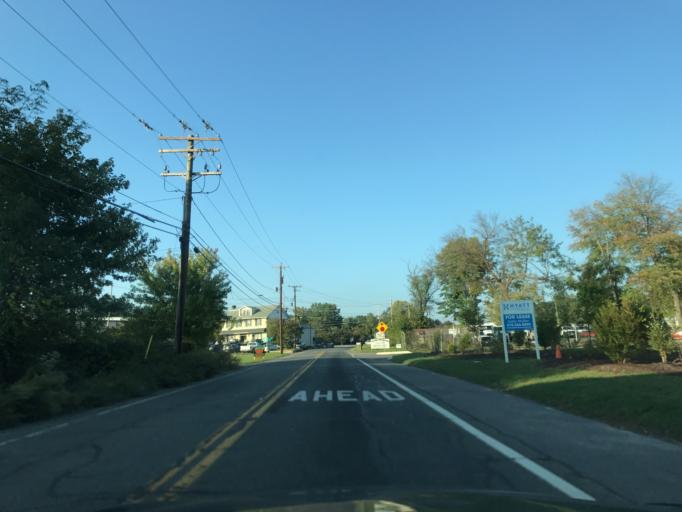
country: US
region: Maryland
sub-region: Anne Arundel County
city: Gambrills
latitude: 39.0718
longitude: -76.6305
